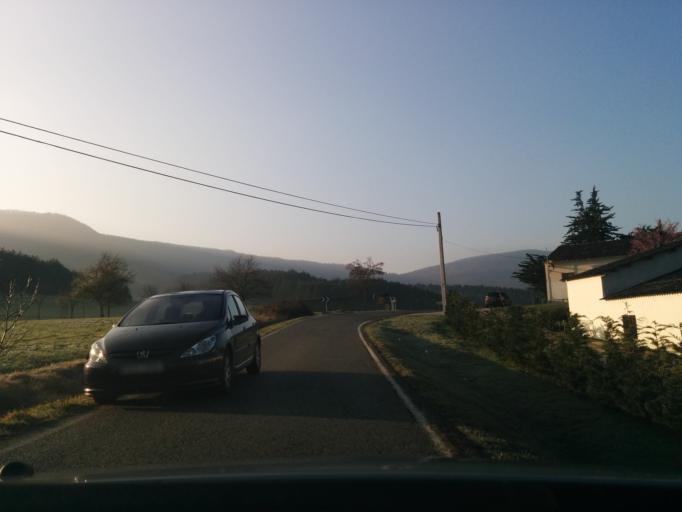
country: ES
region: Navarre
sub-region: Provincia de Navarra
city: Elorz
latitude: 42.7765
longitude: -1.5298
